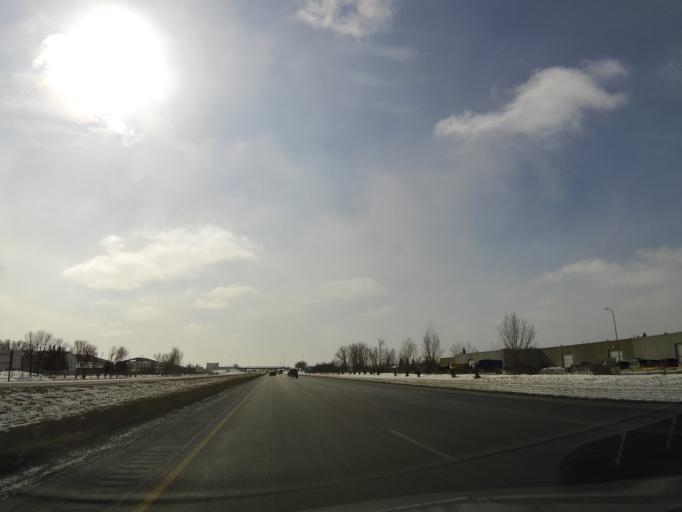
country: US
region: North Dakota
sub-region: Grand Forks County
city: Grand Forks
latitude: 47.9290
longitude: -97.0937
